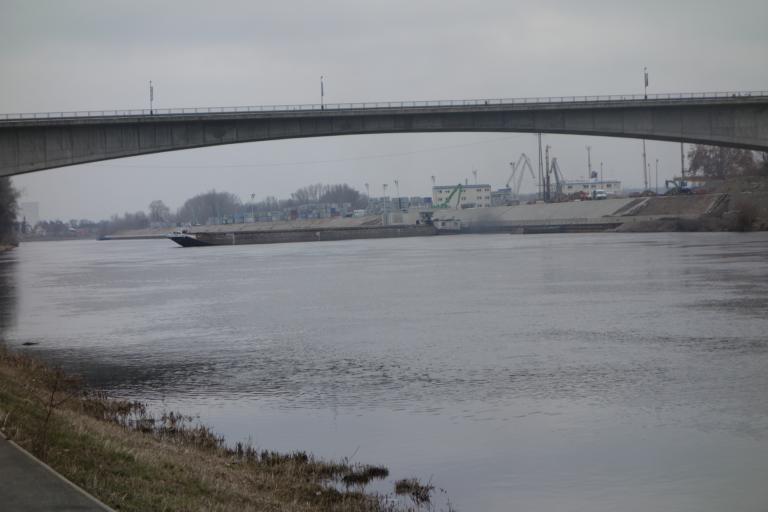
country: CZ
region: Central Bohemia
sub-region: Okres Melnik
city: Melnik
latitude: 50.3557
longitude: 14.4627
